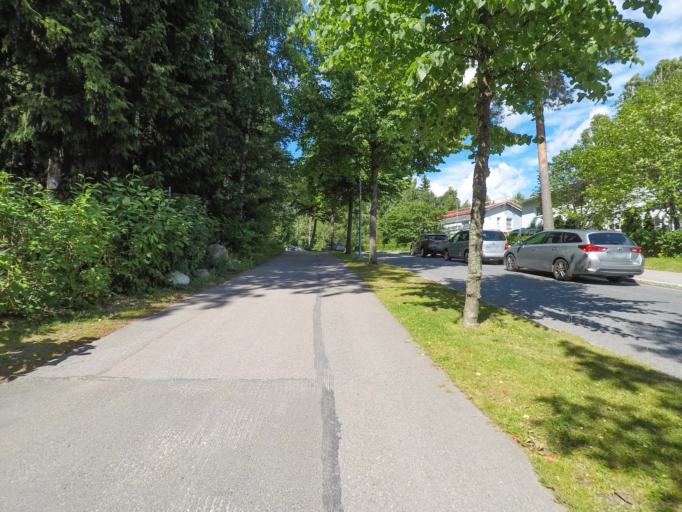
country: FI
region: Uusimaa
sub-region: Helsinki
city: Vantaa
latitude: 60.2202
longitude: 25.0907
